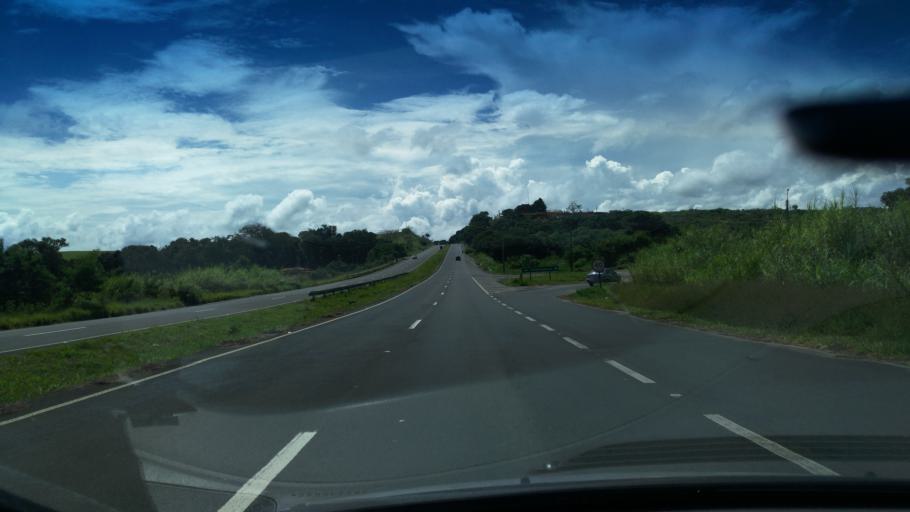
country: BR
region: Sao Paulo
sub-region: Santo Antonio Do Jardim
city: Espirito Santo do Pinhal
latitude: -22.1821
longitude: -46.7591
